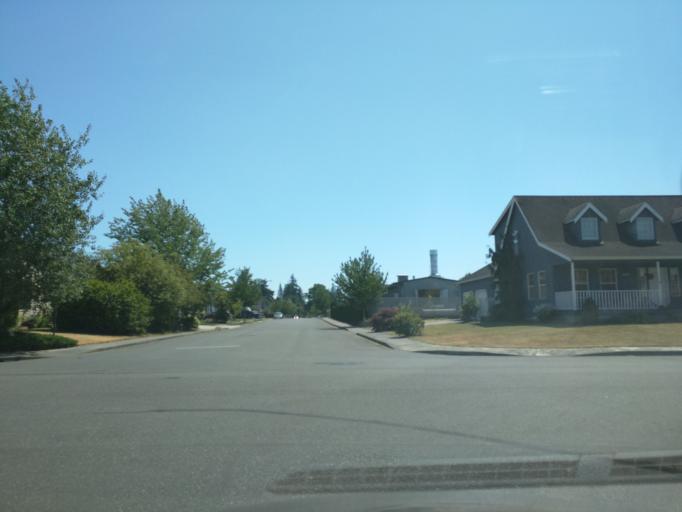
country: US
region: Washington
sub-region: Whatcom County
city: Lynden
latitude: 48.9533
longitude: -122.4605
